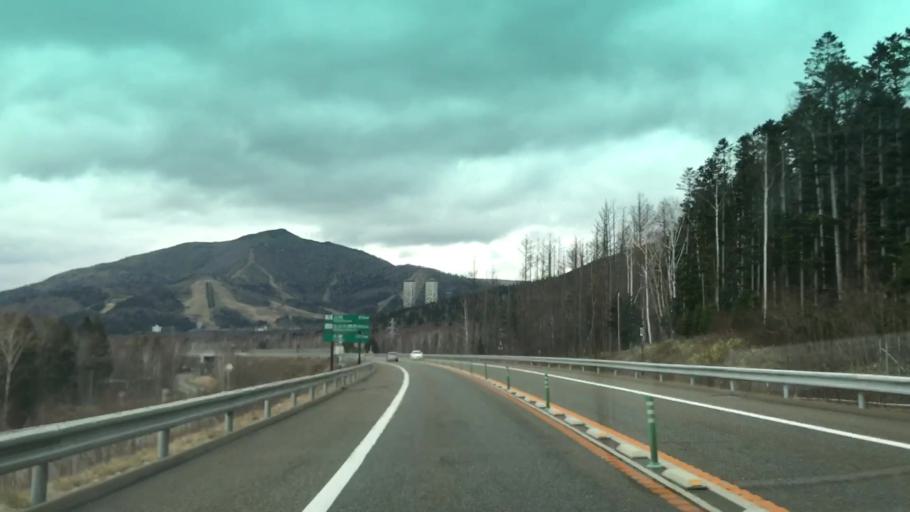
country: JP
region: Hokkaido
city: Shimo-furano
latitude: 43.0502
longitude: 142.6493
